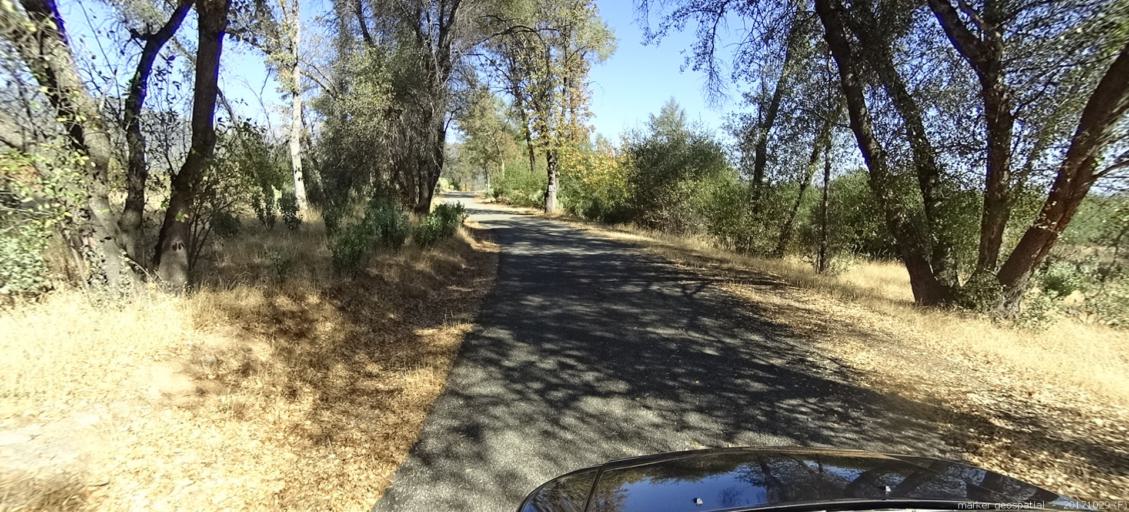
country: US
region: California
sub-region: Shasta County
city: Shasta
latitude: 40.4842
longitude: -122.6231
